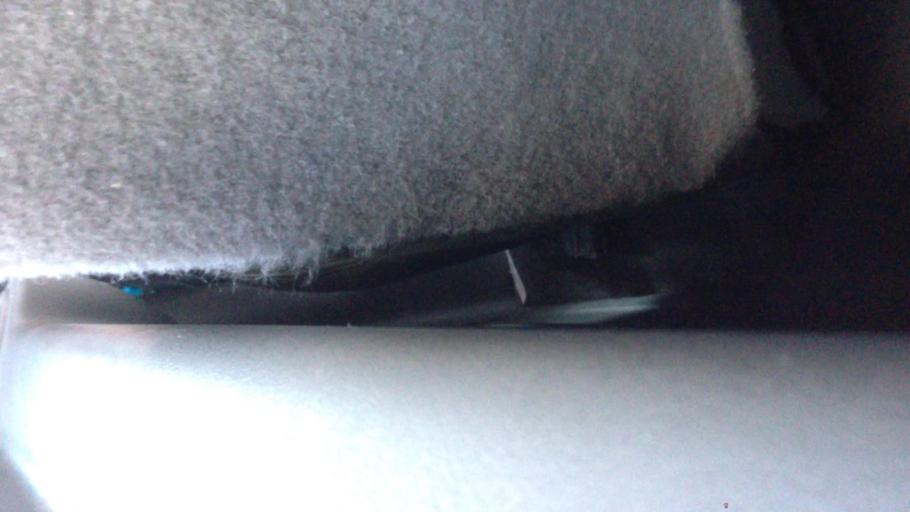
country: US
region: New York
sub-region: Columbia County
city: Lorenz Park
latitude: 42.2575
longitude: -73.7736
